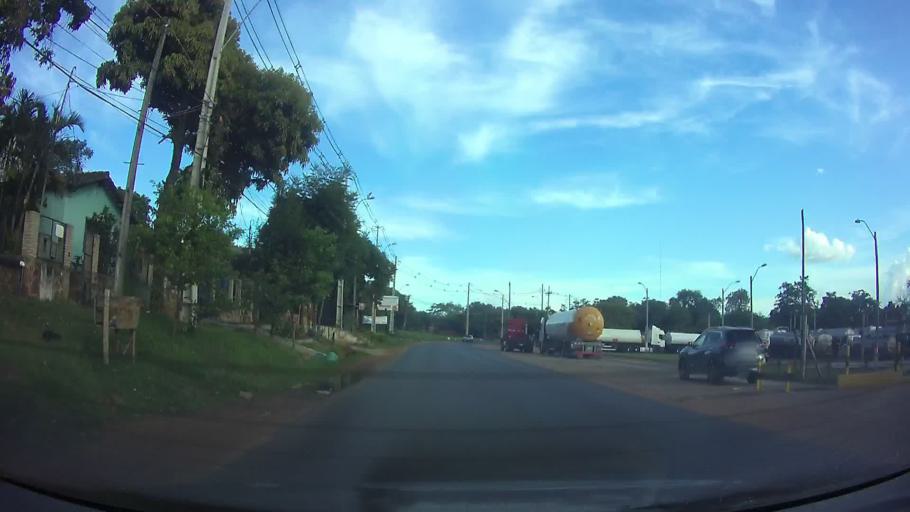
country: PY
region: Central
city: San Antonio
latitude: -25.4305
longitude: -57.5537
